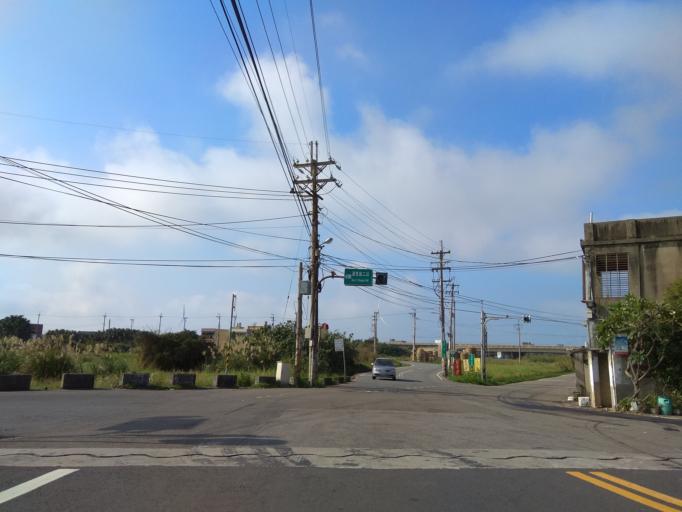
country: TW
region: Taiwan
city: Taoyuan City
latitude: 25.0784
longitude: 121.1735
